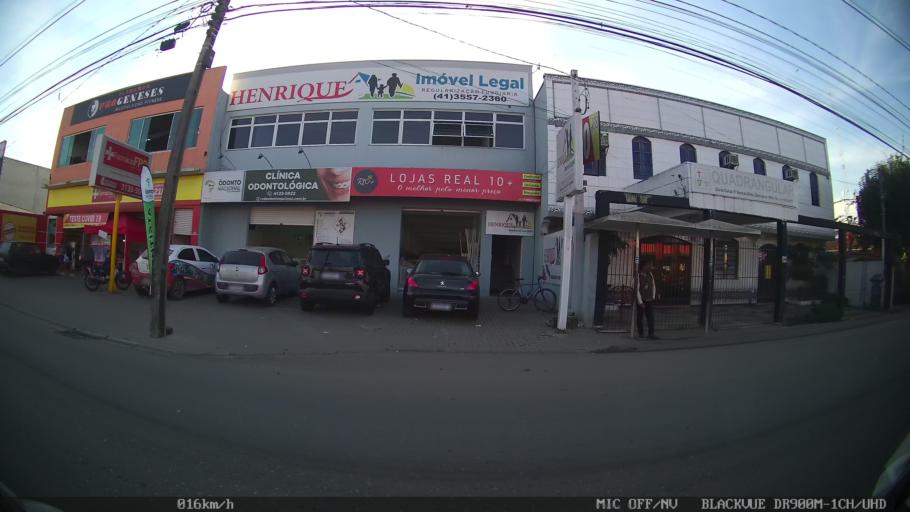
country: BR
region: Parana
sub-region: Pinhais
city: Pinhais
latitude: -25.4542
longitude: -49.1518
